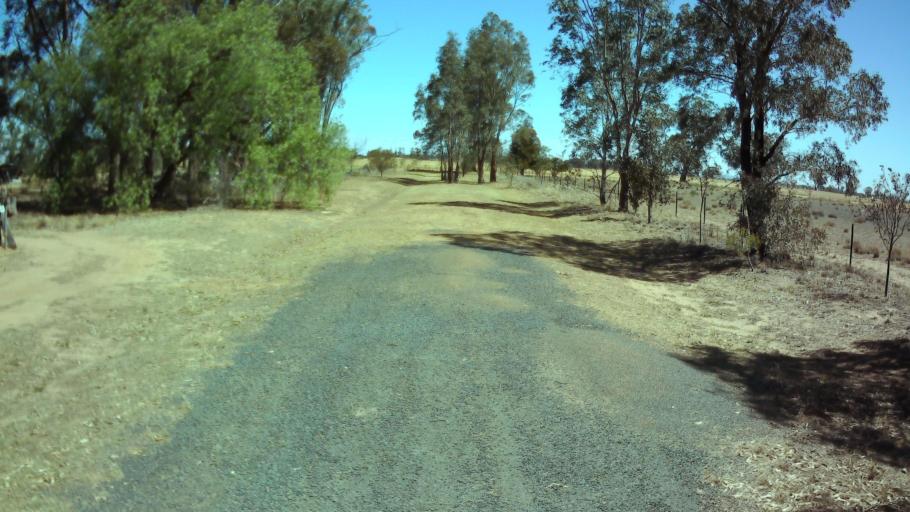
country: AU
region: New South Wales
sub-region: Weddin
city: Grenfell
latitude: -34.0158
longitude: 147.7896
